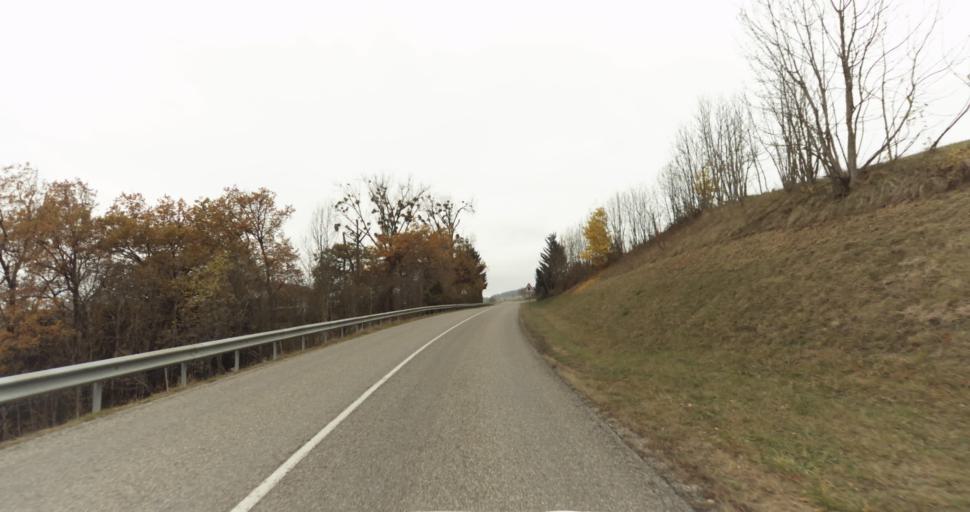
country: FR
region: Rhone-Alpes
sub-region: Departement de la Haute-Savoie
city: Viuz-la-Chiesaz
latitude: 45.8373
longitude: 6.0442
